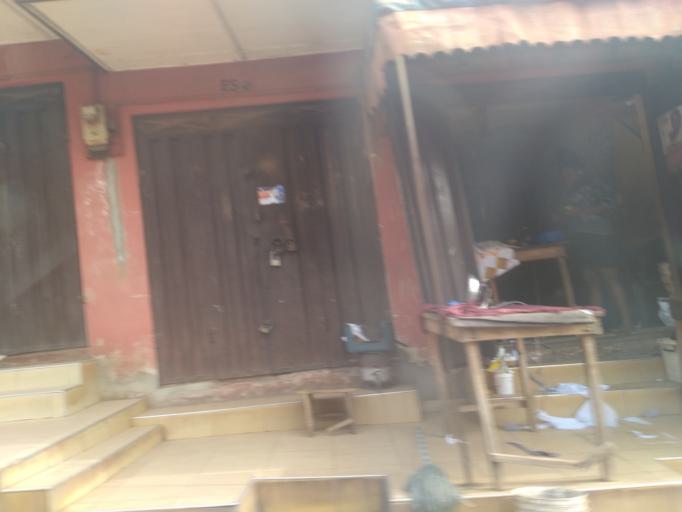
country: GH
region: Ashanti
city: Kumasi
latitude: 6.7019
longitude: -1.6188
